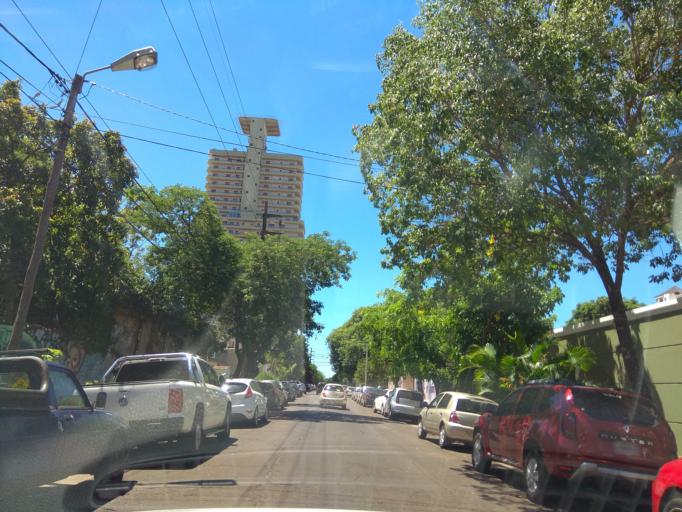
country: AR
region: Misiones
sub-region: Departamento de Capital
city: Posadas
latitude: -27.3626
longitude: -55.8908
